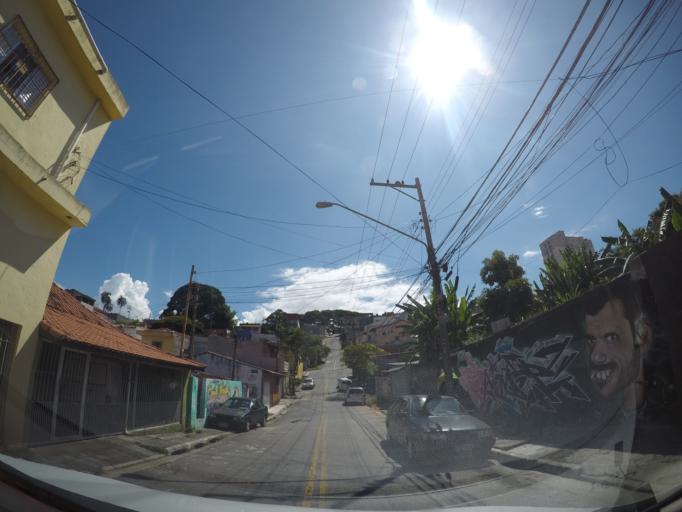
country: BR
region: Sao Paulo
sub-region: Guarulhos
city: Guarulhos
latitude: -23.4578
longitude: -46.5407
